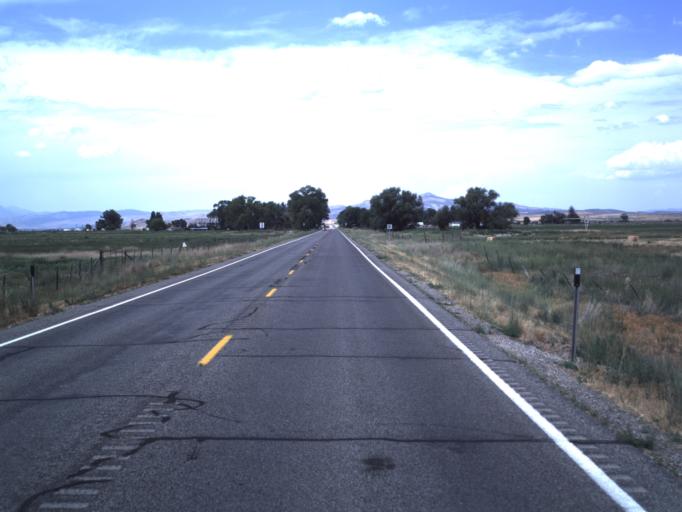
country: US
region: Utah
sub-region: Sanpete County
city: Moroni
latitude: 39.4664
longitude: -111.5627
